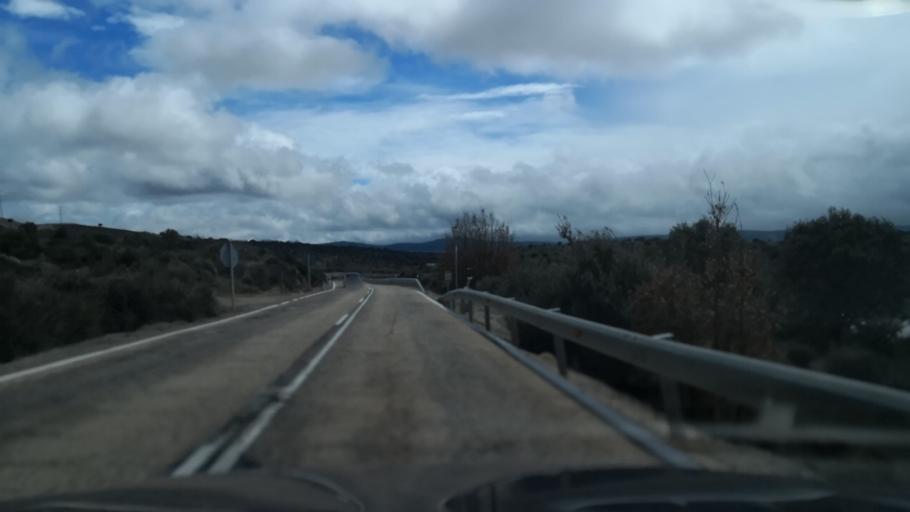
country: ES
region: Castille and Leon
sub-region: Provincia de Zamora
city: Villardeciervos
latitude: 41.9859
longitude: -6.2366
